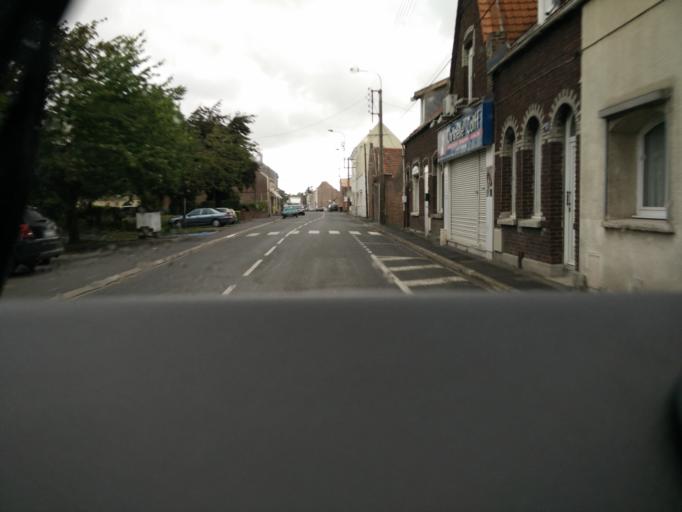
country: FR
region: Nord-Pas-de-Calais
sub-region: Departement du Pas-de-Calais
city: Grenay
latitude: 50.4503
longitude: 2.7398
